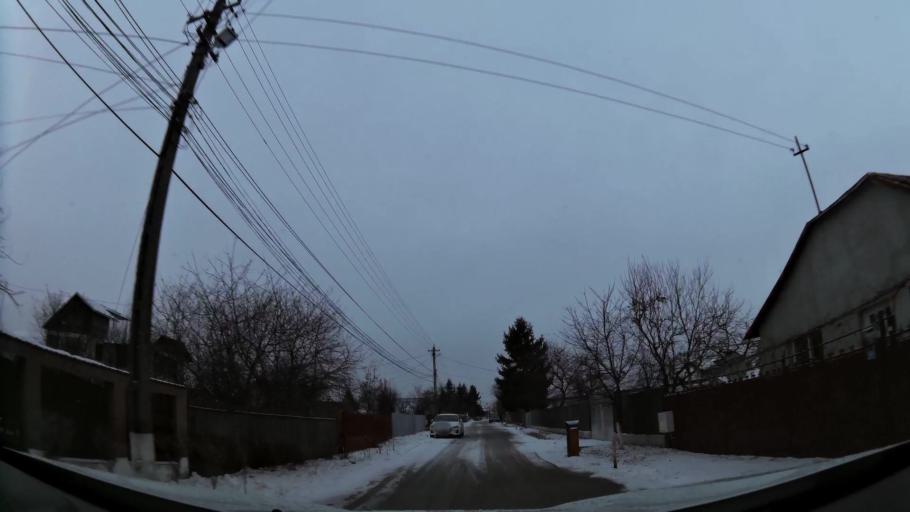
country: RO
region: Prahova
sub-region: Comuna Berceni
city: Corlatesti
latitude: 44.9118
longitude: 26.0926
